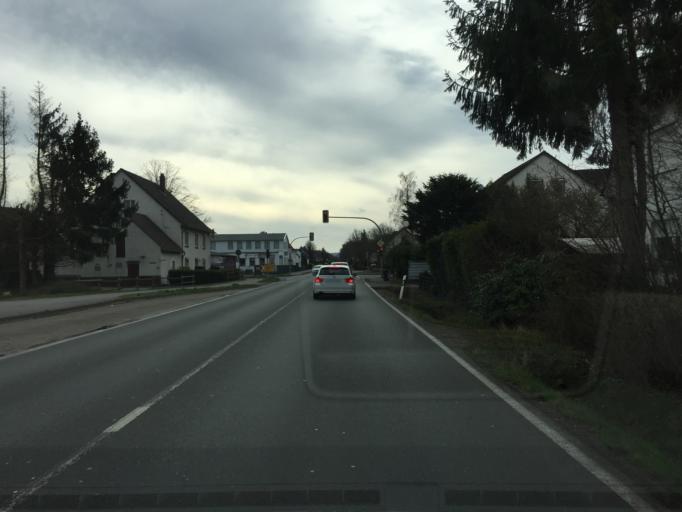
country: DE
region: North Rhine-Westphalia
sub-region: Regierungsbezirk Detmold
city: Lage
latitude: 52.0164
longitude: 8.7662
